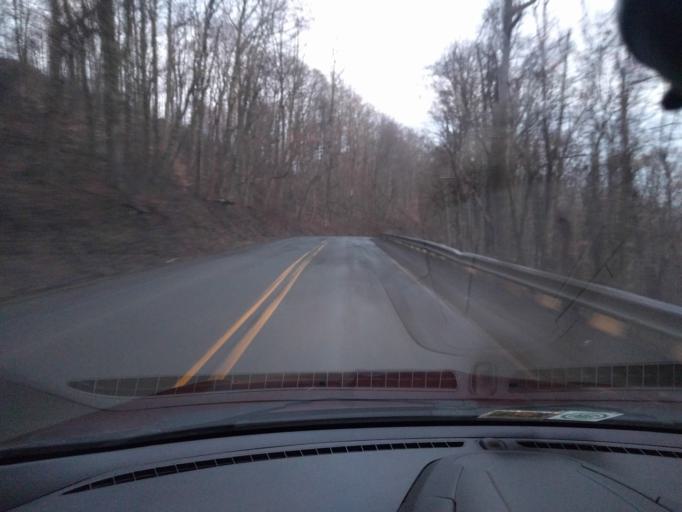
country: US
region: West Virginia
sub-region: Greenbrier County
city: Rainelle
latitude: 37.9865
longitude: -80.8533
